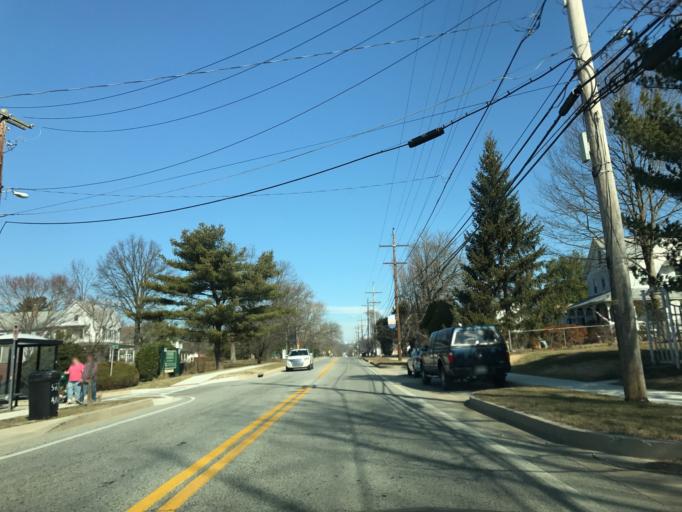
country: US
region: Maryland
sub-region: Cecil County
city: Perryville
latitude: 39.5621
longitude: -76.0712
